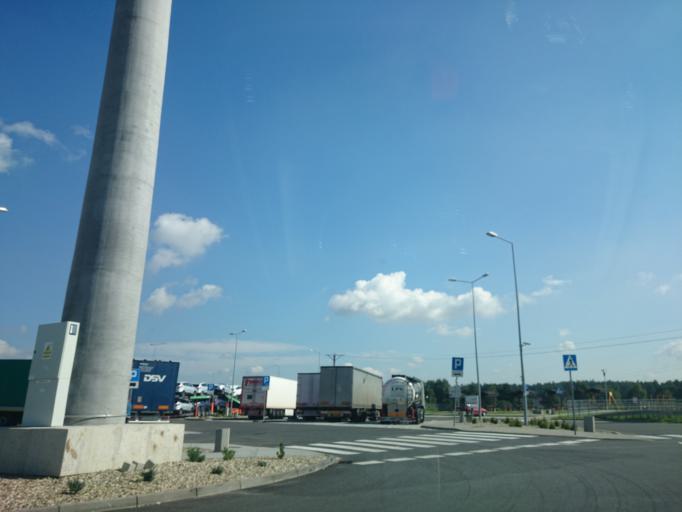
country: PL
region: Silesian Voivodeship
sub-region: Zory
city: Zory
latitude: 50.0755
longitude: 18.6645
